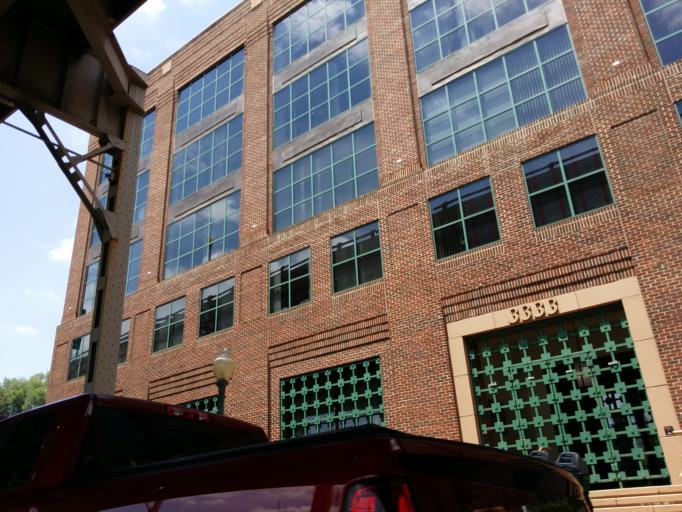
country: US
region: Washington, D.C.
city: Washington, D.C.
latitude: 38.9039
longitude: -77.0673
